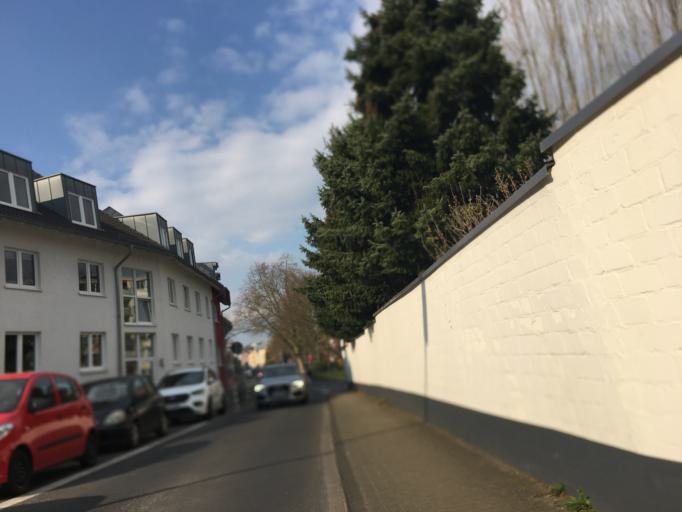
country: DE
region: North Rhine-Westphalia
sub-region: Regierungsbezirk Koln
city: Nippes
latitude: 50.9812
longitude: 6.9445
